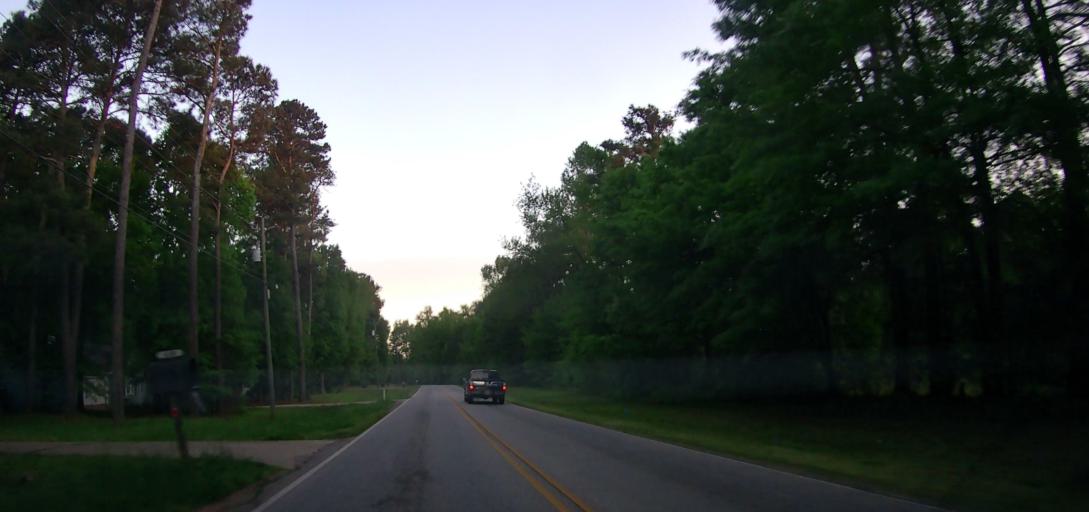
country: US
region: Georgia
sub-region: Henry County
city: McDonough
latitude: 33.4406
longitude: -84.1877
